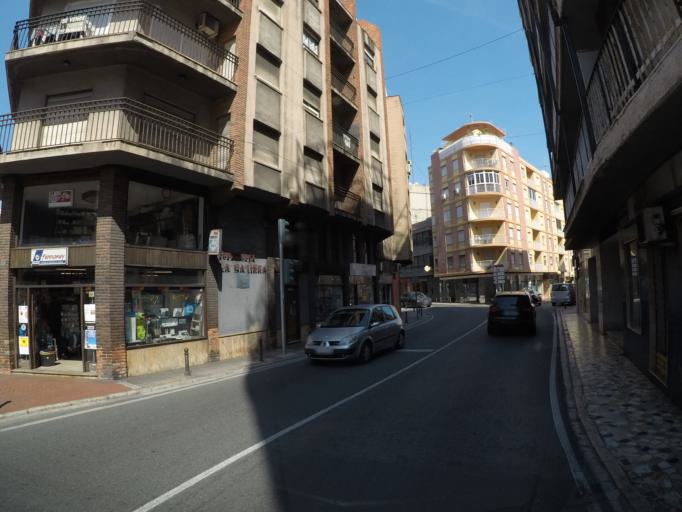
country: ES
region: Valencia
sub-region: Provincia de Valencia
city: Oliva
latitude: 38.9189
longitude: -0.1180
